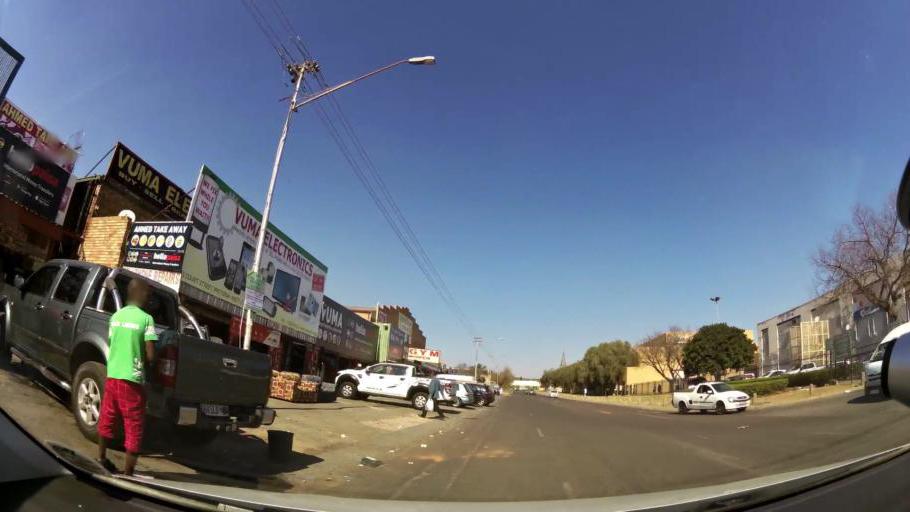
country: ZA
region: Gauteng
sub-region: City of Tshwane Metropolitan Municipality
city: Pretoria
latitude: -25.7462
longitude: 28.1500
